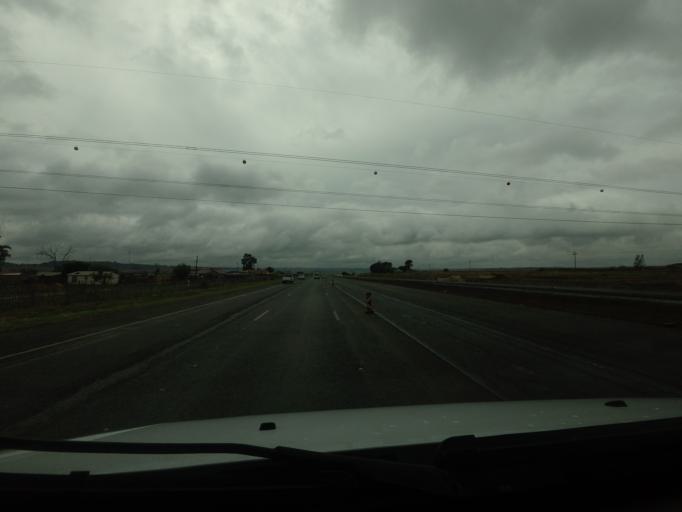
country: ZA
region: Mpumalanga
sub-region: Nkangala District Municipality
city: Witbank
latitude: -25.8744
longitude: 29.1400
